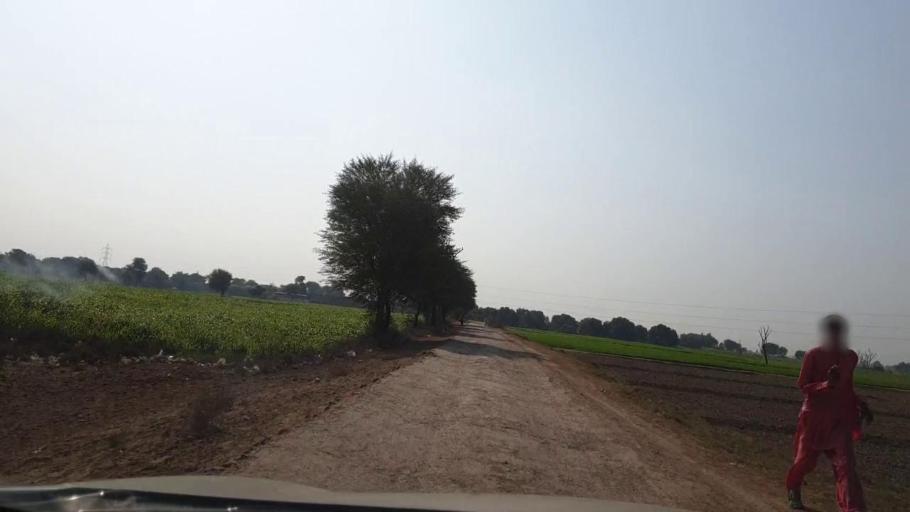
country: PK
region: Sindh
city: Bhit Shah
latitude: 25.7506
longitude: 68.5054
